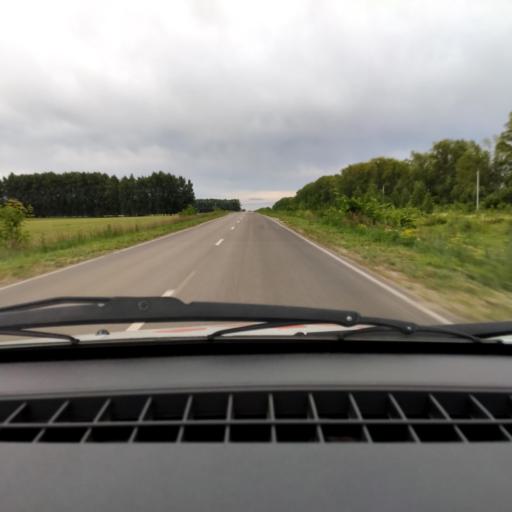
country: RU
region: Bashkortostan
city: Avdon
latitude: 54.5319
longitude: 55.7653
